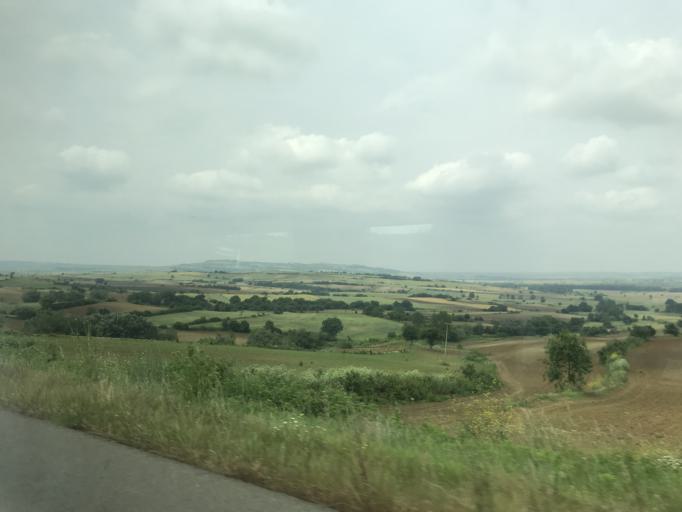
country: TR
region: Tekirdag
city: Inecik
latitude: 40.9367
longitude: 27.2633
